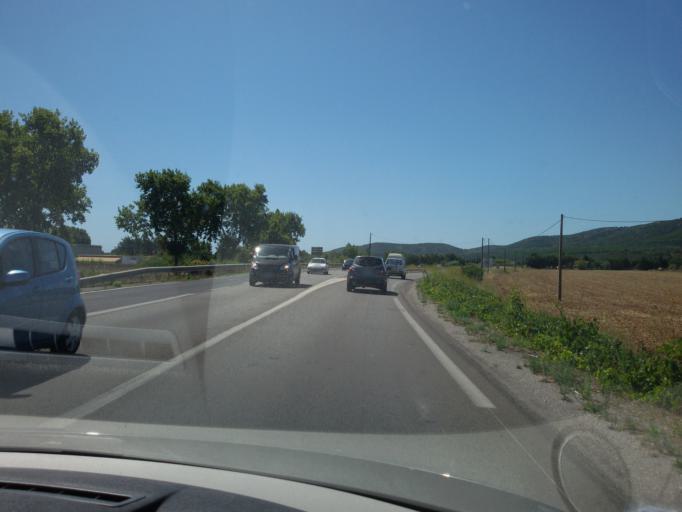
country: FR
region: Languedoc-Roussillon
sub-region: Departement de l'Herault
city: Mireval
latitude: 43.5036
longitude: 3.7903
